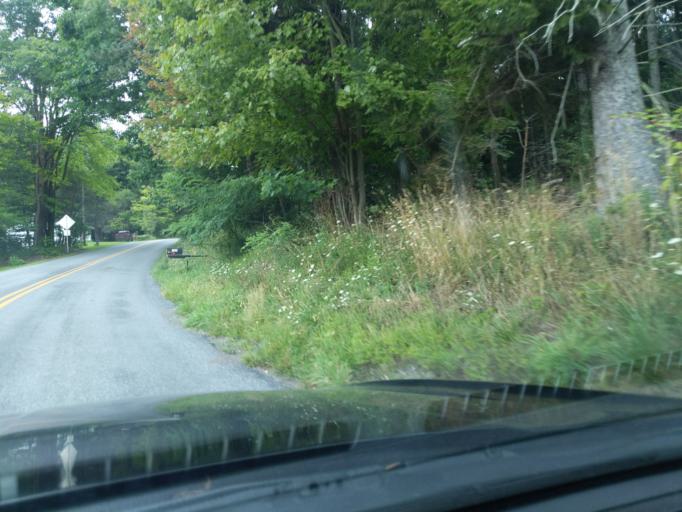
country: US
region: Pennsylvania
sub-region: Cambria County
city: Portage
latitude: 40.3439
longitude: -78.5864
